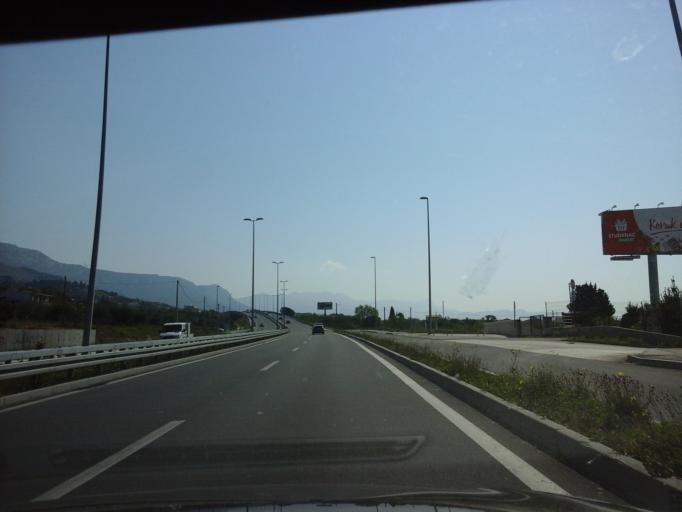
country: HR
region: Splitsko-Dalmatinska
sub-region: Grad Split
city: Split
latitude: 43.5573
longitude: 16.3739
